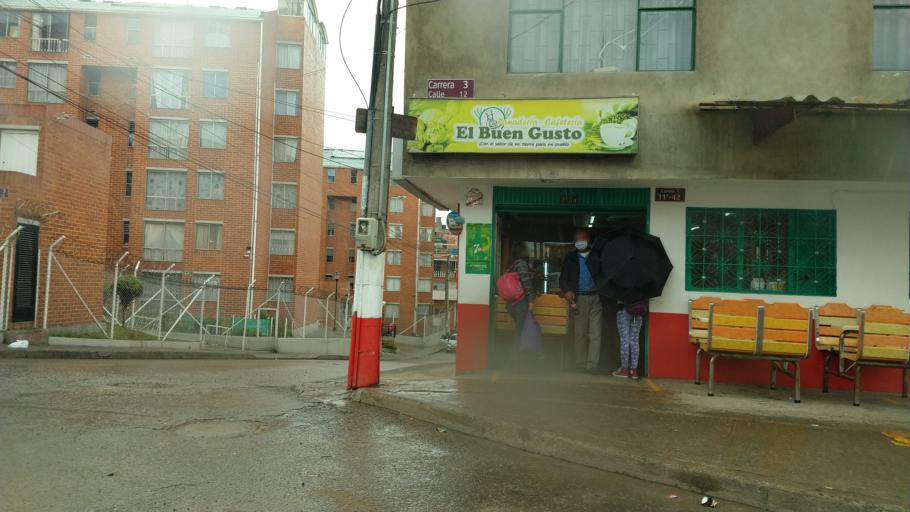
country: CO
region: Cundinamarca
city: Soacha
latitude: 4.5769
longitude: -74.2185
